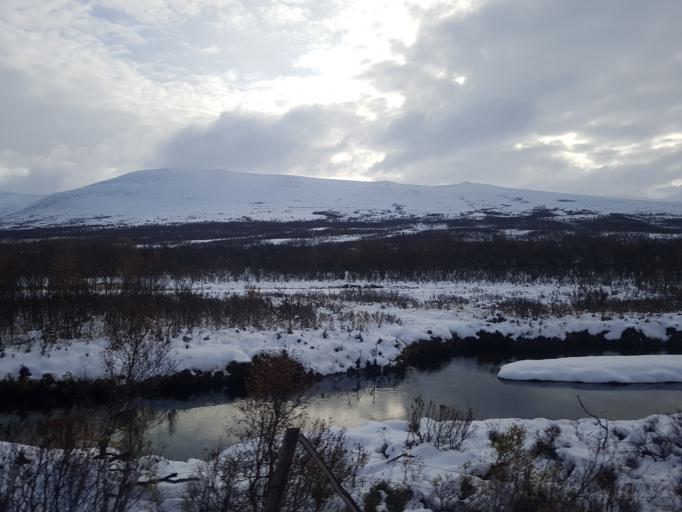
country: NO
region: Oppland
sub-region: Dovre
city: Dovre
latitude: 62.1249
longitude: 9.3028
